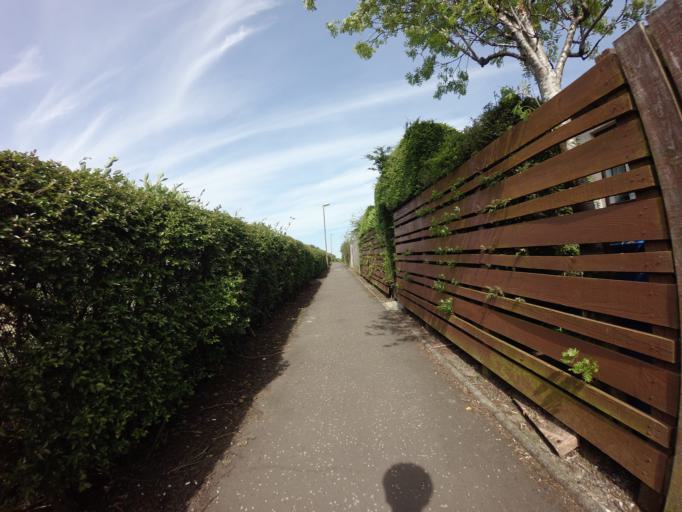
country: GB
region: Scotland
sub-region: West Lothian
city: Livingston
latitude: 55.9098
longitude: -3.5297
